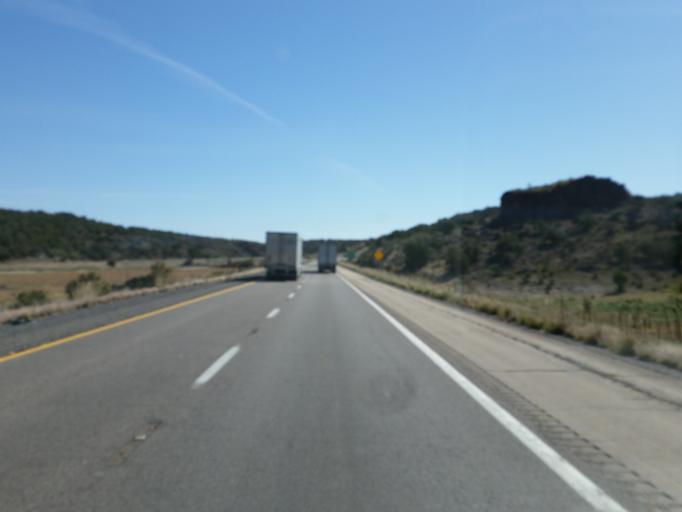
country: US
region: Arizona
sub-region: Mohave County
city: Peach Springs
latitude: 35.1850
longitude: -113.4491
